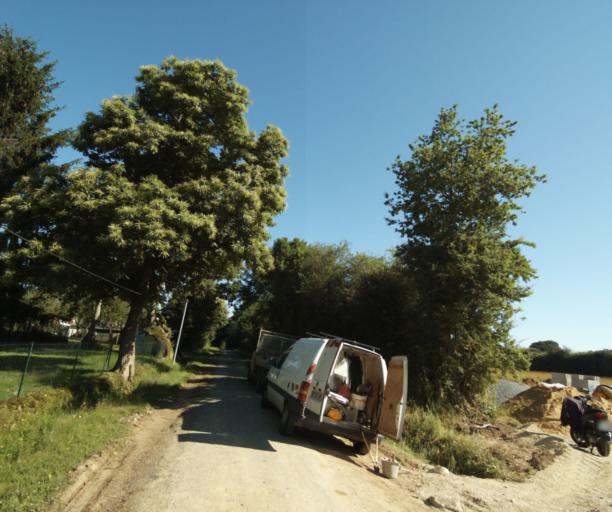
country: FR
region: Pays de la Loire
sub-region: Departement de la Mayenne
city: Laval
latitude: 48.0405
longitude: -0.7333
